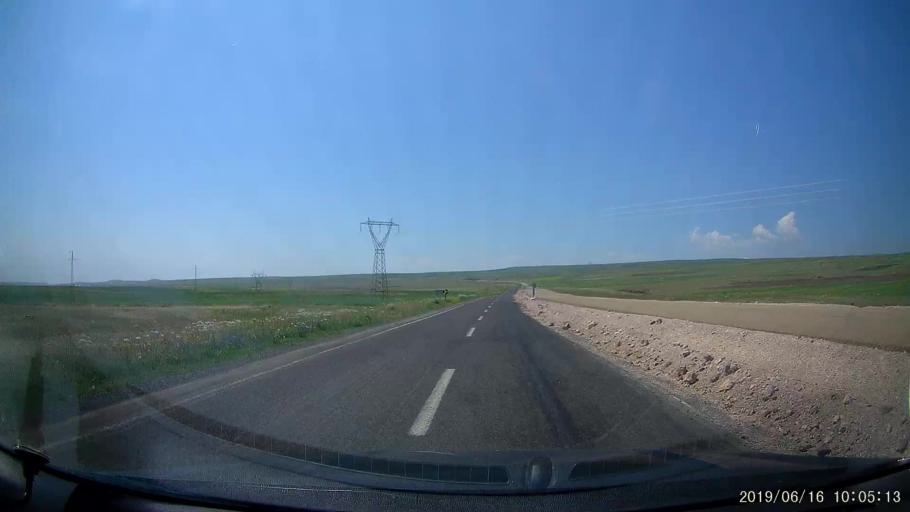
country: TR
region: Kars
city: Digor
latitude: 40.2735
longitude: 43.5377
